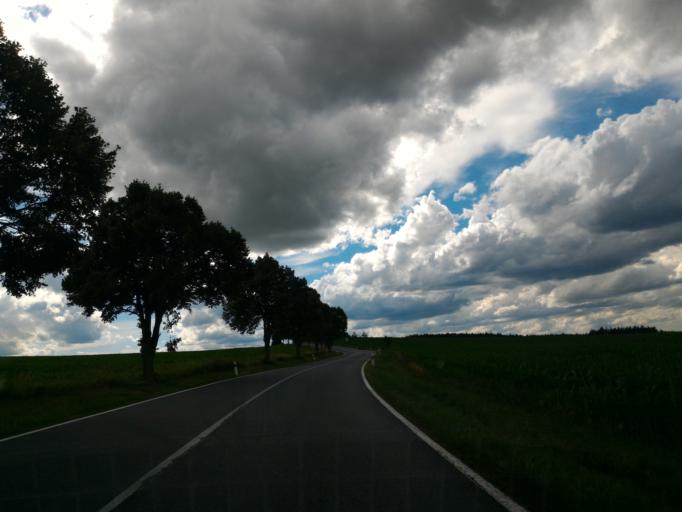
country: CZ
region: Vysocina
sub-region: Okres Jihlava
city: Polna
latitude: 49.4419
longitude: 15.7529
